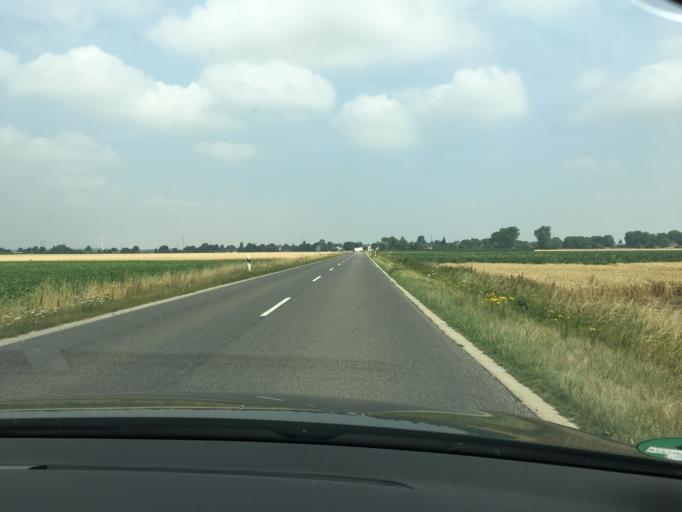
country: DE
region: North Rhine-Westphalia
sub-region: Regierungsbezirk Koln
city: Merzenich
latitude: 50.8285
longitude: 6.5842
